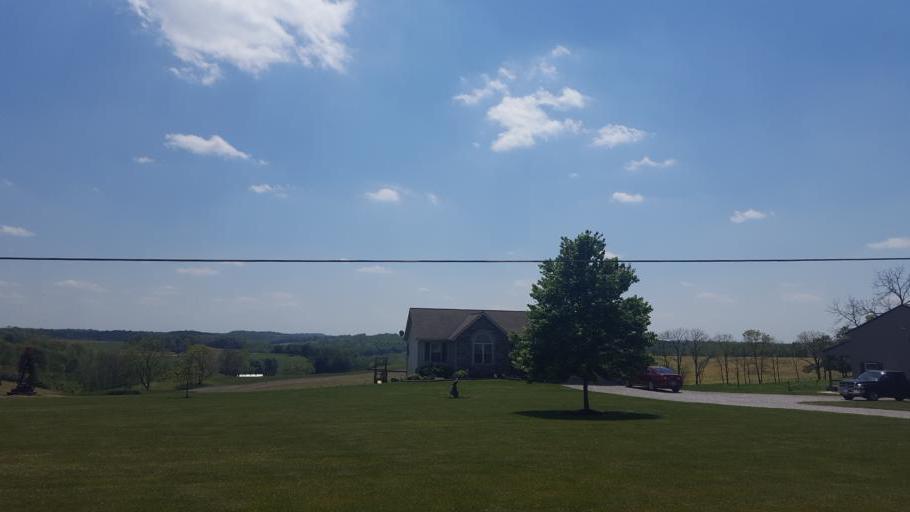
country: US
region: Ohio
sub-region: Knox County
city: Oak Hill
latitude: 40.2853
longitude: -82.2658
